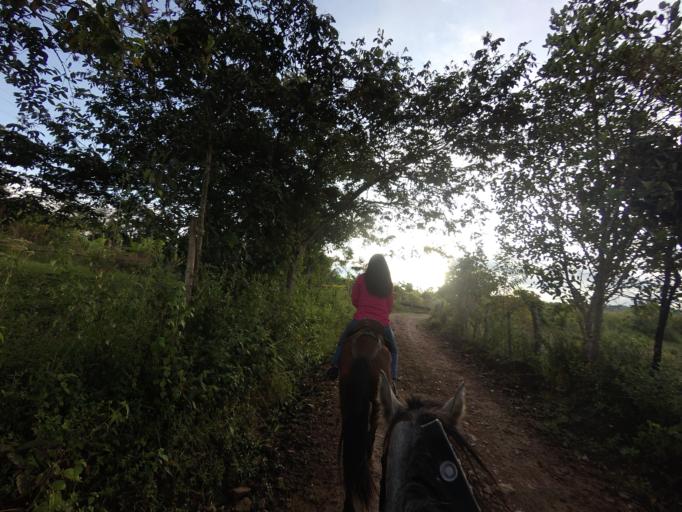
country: CO
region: Huila
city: San Agustin
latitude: 1.9023
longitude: -76.2715
